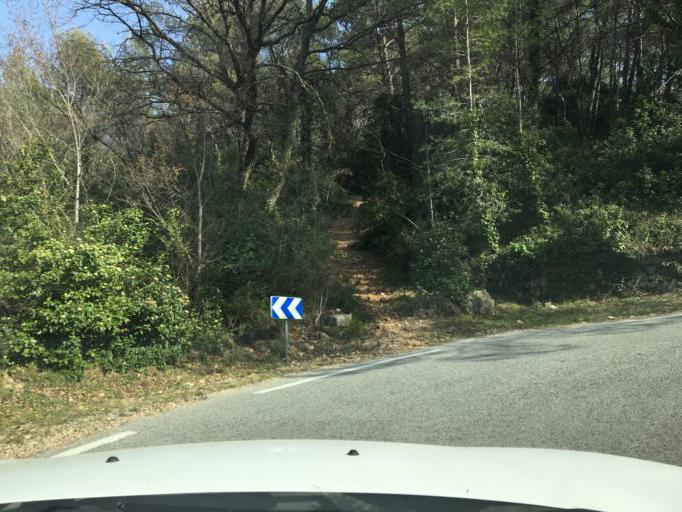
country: FR
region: Provence-Alpes-Cote d'Azur
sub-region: Departement du Var
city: Draguignan
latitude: 43.5429
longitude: 6.4891
